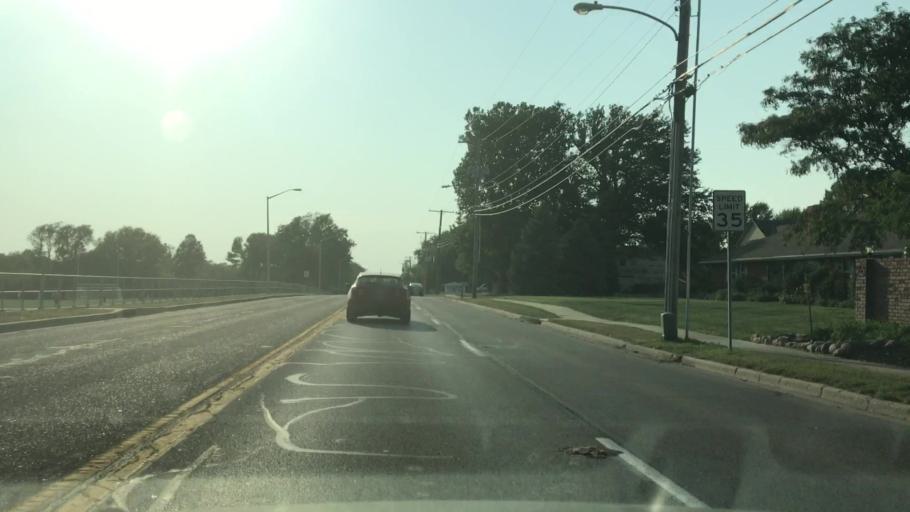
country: US
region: Kansas
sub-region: Johnson County
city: Lenexa
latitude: 38.9928
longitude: -94.7259
